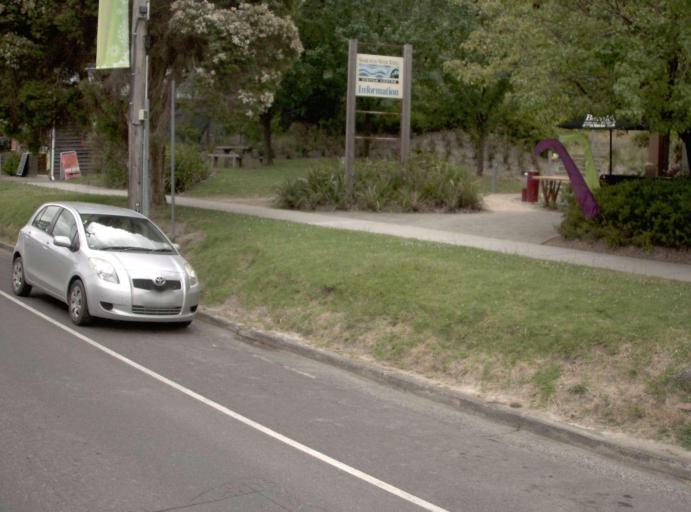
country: AU
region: Victoria
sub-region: Yarra Ranges
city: Millgrove
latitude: -37.7536
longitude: 145.6895
